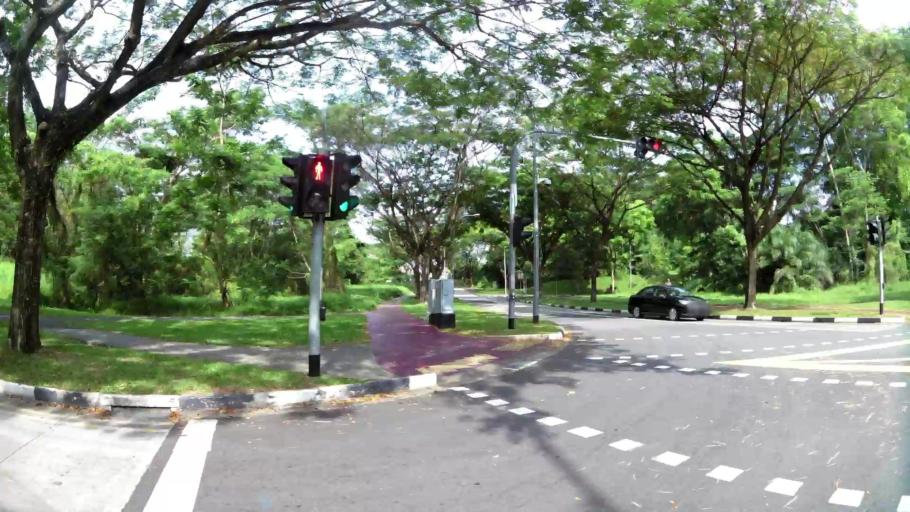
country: SG
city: Singapore
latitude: 1.2997
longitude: 103.7919
